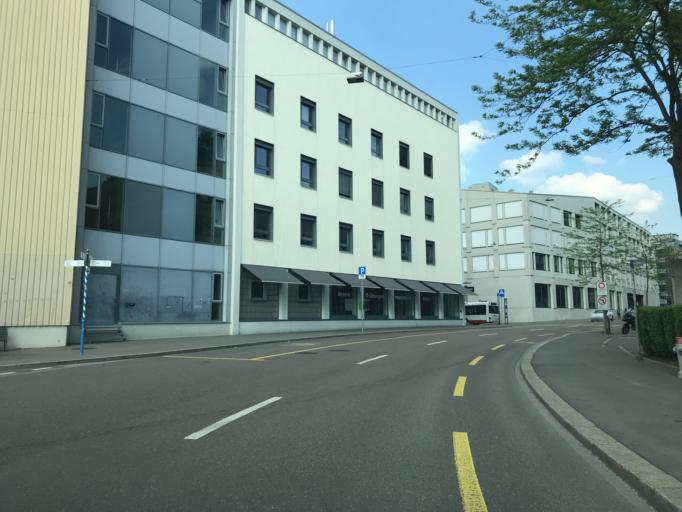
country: CH
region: Zurich
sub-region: Bezirk Winterthur
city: Stadt Winterthur (Kreis 1) / Heiligberg
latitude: 47.4975
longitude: 8.7226
